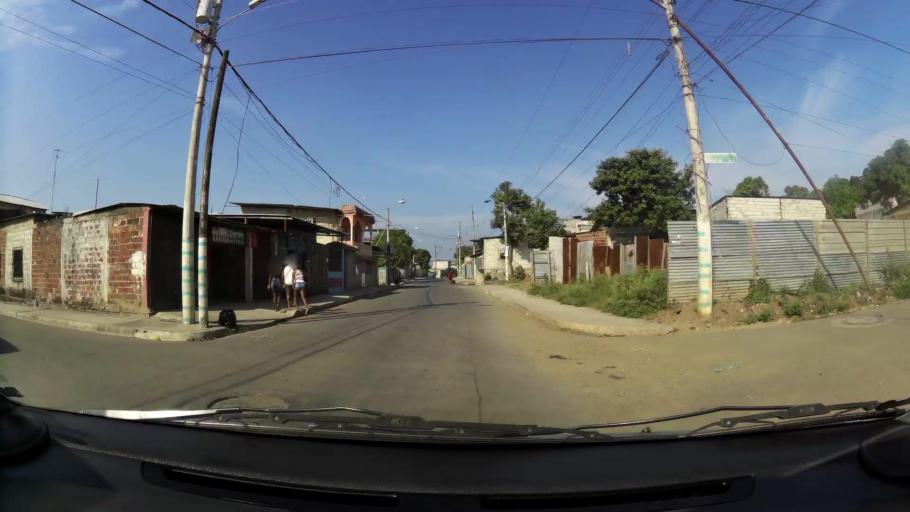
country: EC
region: Guayas
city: Eloy Alfaro
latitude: -2.0806
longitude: -79.9271
